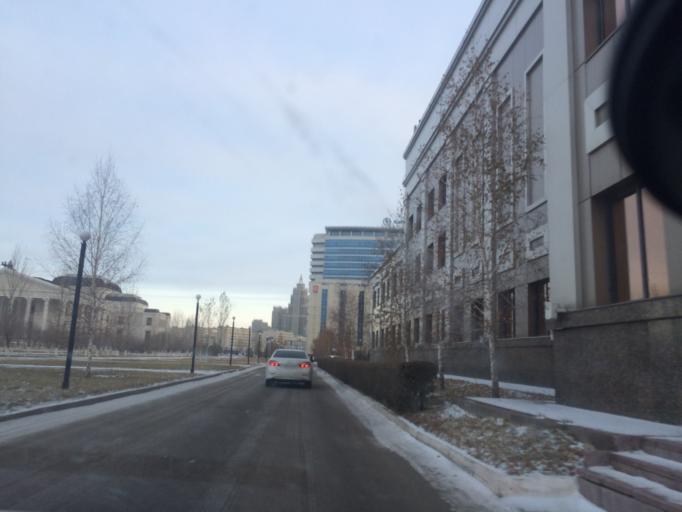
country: KZ
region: Astana Qalasy
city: Astana
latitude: 51.1314
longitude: 71.4115
